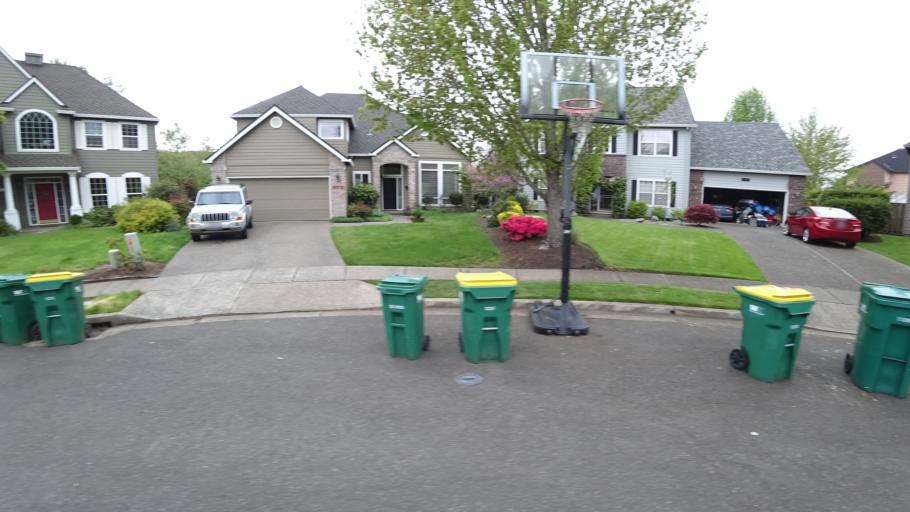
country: US
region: Oregon
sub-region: Washington County
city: Beaverton
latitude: 45.4556
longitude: -122.8324
